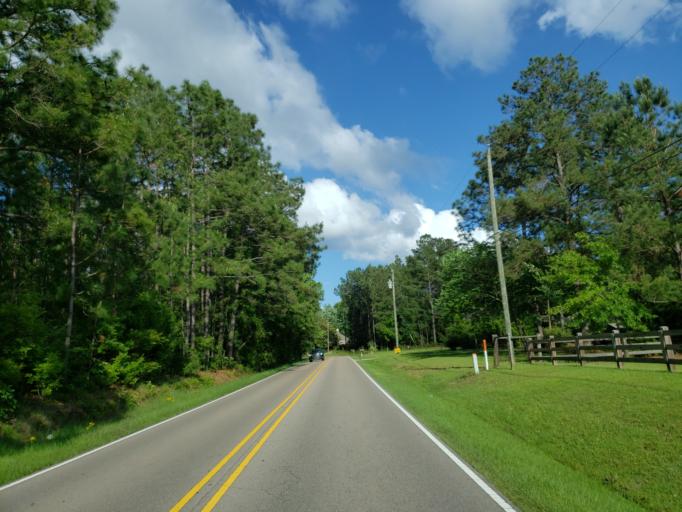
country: US
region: Mississippi
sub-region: Lamar County
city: West Hattiesburg
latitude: 31.2716
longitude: -89.3609
